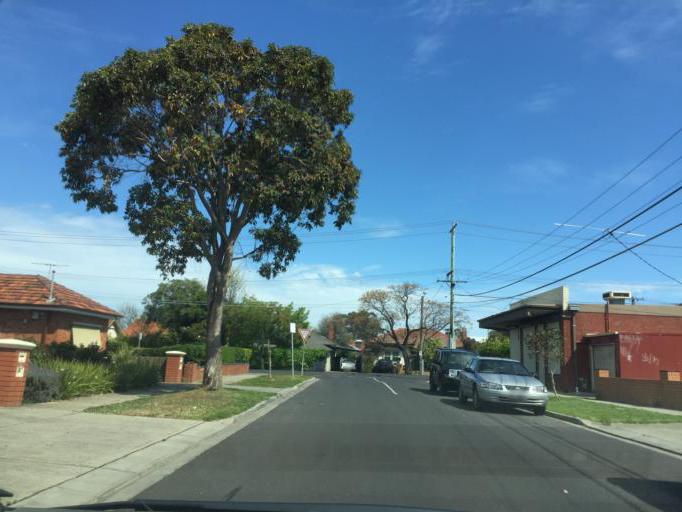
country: AU
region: Victoria
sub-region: Maribyrnong
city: Maribyrnong
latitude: -37.7830
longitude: 144.8876
